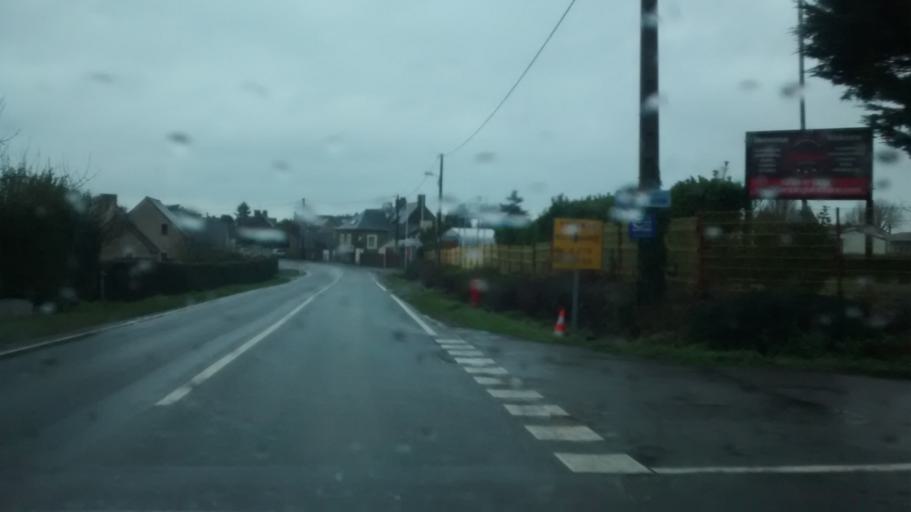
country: FR
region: Brittany
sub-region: Departement d'Ille-et-Vilaine
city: Saint-Coulomb
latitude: 48.6572
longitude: -1.9579
